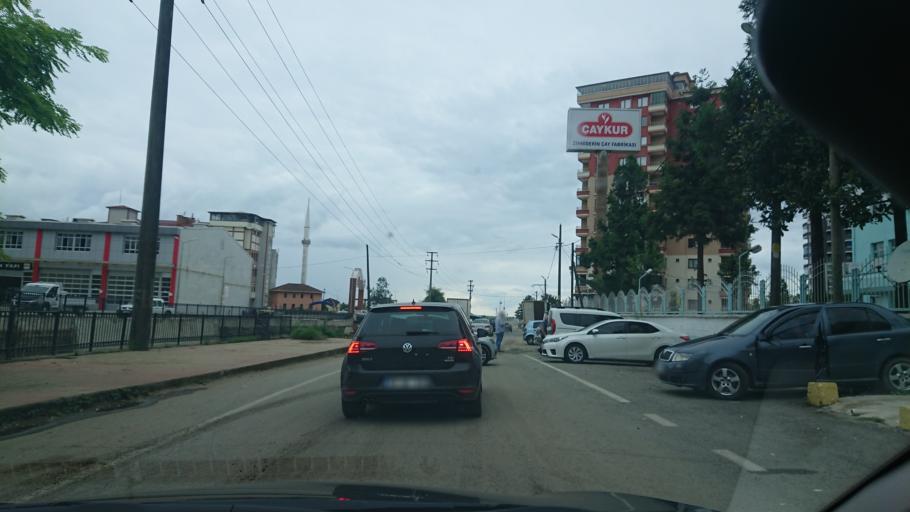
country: TR
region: Rize
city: Rize
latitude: 41.0332
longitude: 40.4815
